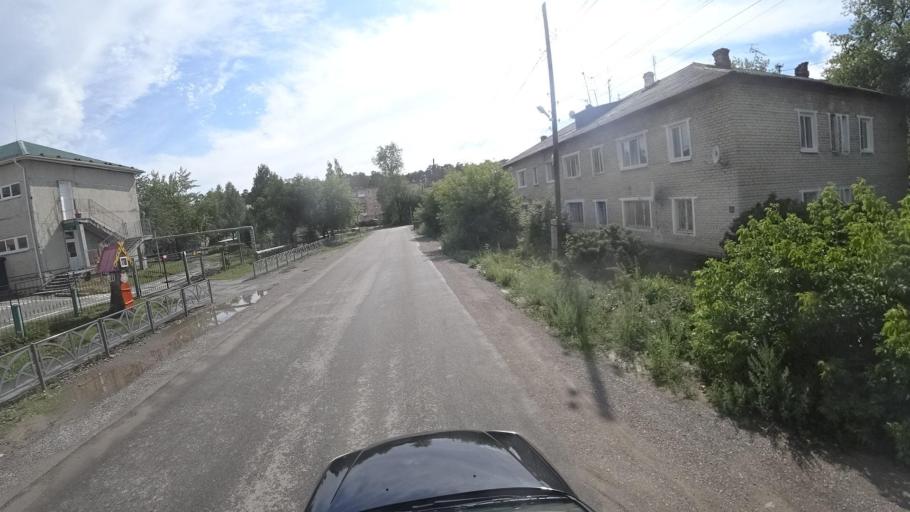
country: RU
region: Sverdlovsk
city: Kamyshlov
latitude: 56.8360
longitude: 62.7334
